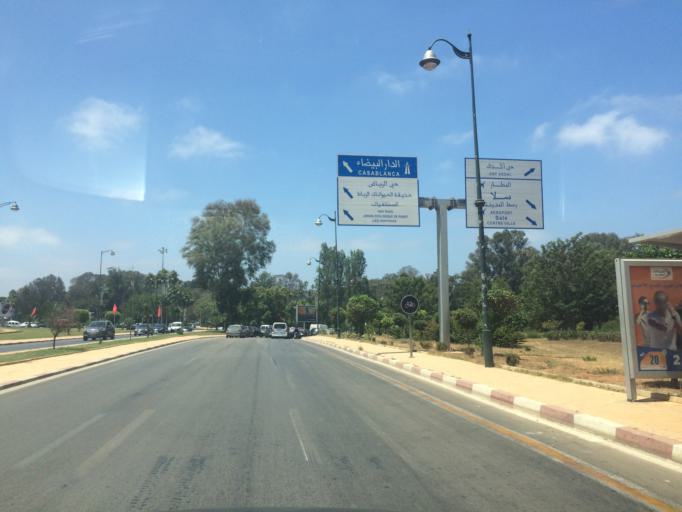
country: MA
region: Rabat-Sale-Zemmour-Zaer
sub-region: Rabat
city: Rabat
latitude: 33.9934
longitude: -6.8367
